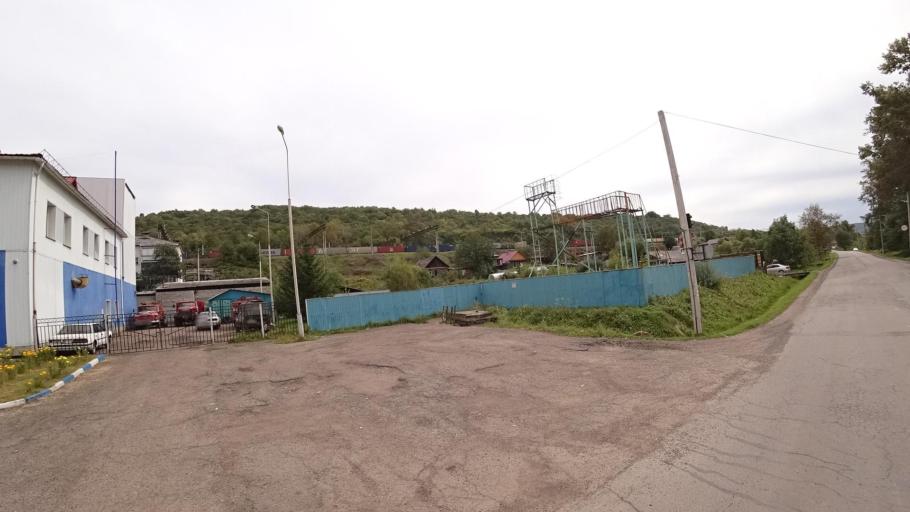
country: RU
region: Jewish Autonomous Oblast
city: Khingansk
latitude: 49.0081
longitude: 131.0572
